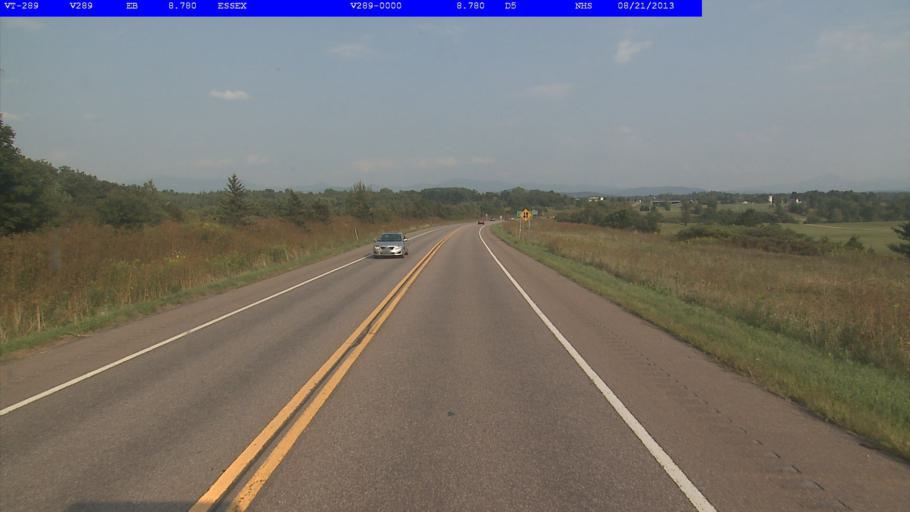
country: US
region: Vermont
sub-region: Chittenden County
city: Essex Junction
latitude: 44.5131
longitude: -73.0988
